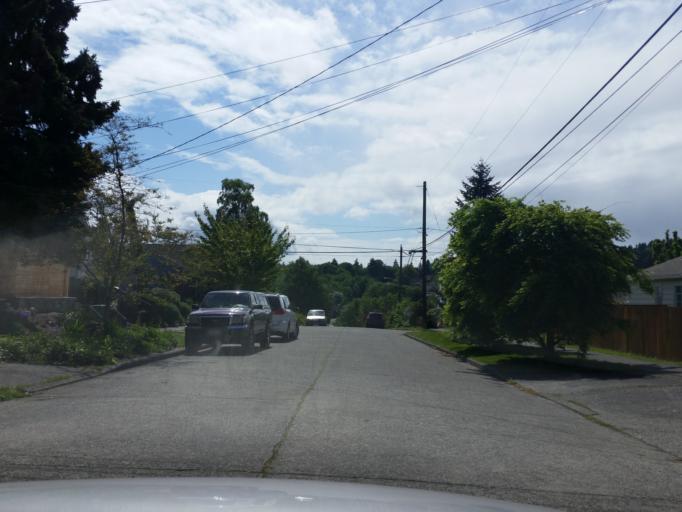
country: US
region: Washington
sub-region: King County
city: Seattle
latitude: 47.6700
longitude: -122.4012
